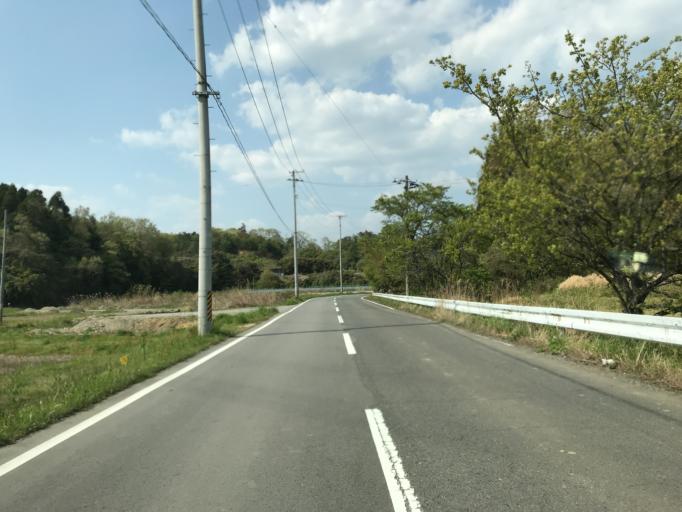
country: JP
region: Fukushima
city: Iwaki
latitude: 36.9659
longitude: 140.7569
